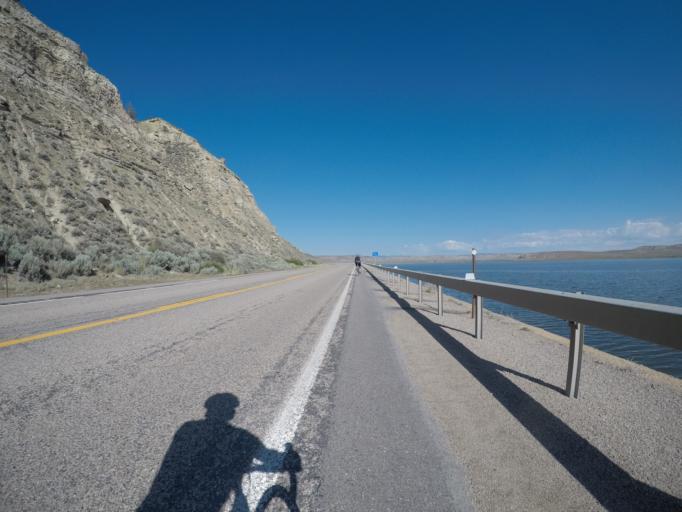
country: US
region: Wyoming
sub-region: Sublette County
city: Marbleton
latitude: 42.1157
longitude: -110.1589
